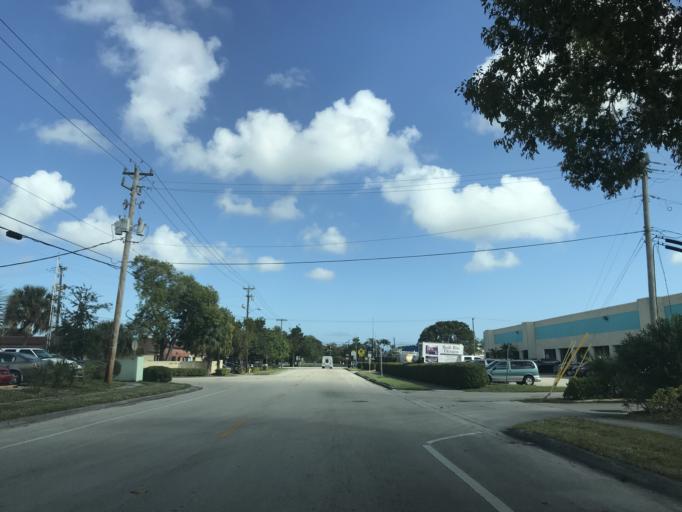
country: US
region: Florida
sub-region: Broward County
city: Margate
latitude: 26.2486
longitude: -80.1960
